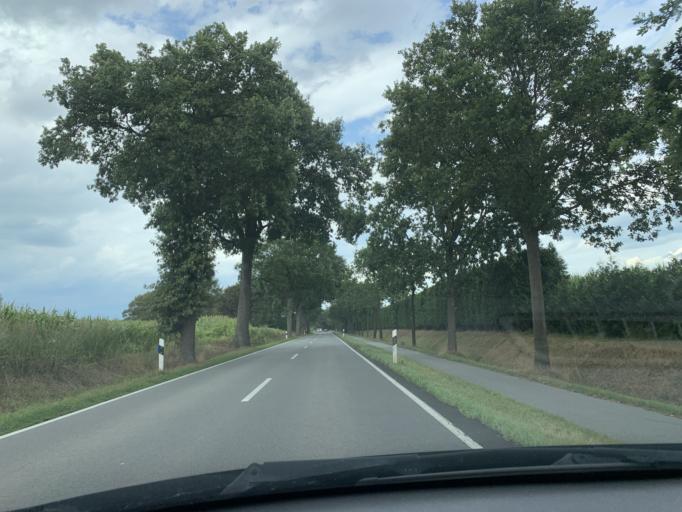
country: DE
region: Lower Saxony
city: Westerstede
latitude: 53.2312
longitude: 7.9030
